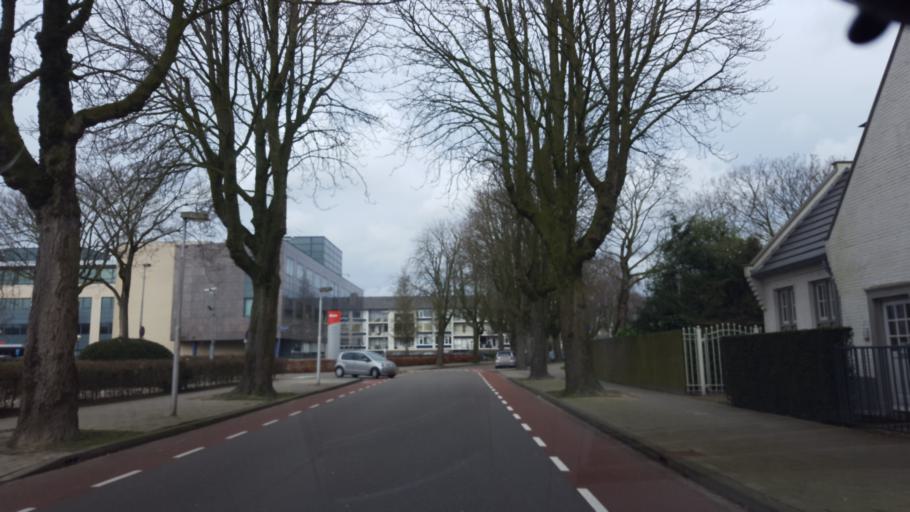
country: NL
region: North Brabant
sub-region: Gemeente Eindhoven
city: Meerhoven
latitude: 51.4392
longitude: 5.4312
